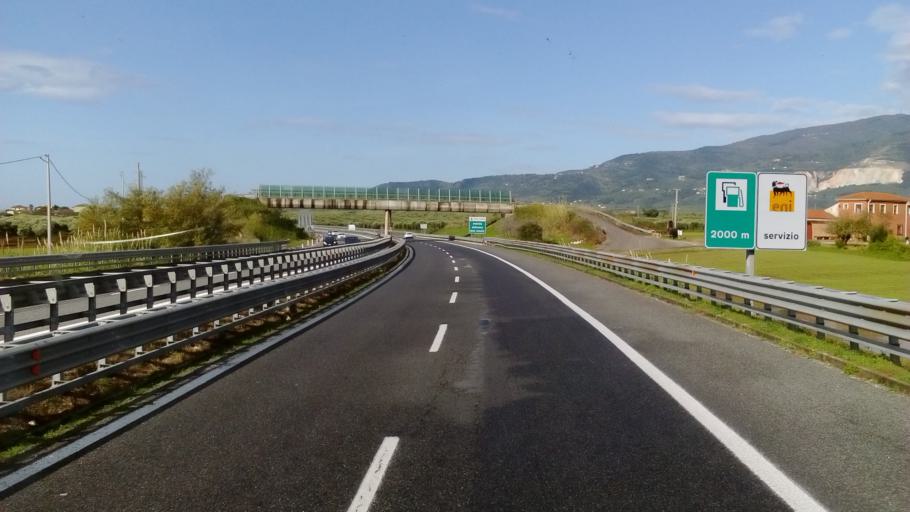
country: IT
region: Calabria
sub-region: Provincia di Catanzaro
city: Santa Eufemia Lamezia
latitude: 38.9220
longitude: 16.2615
